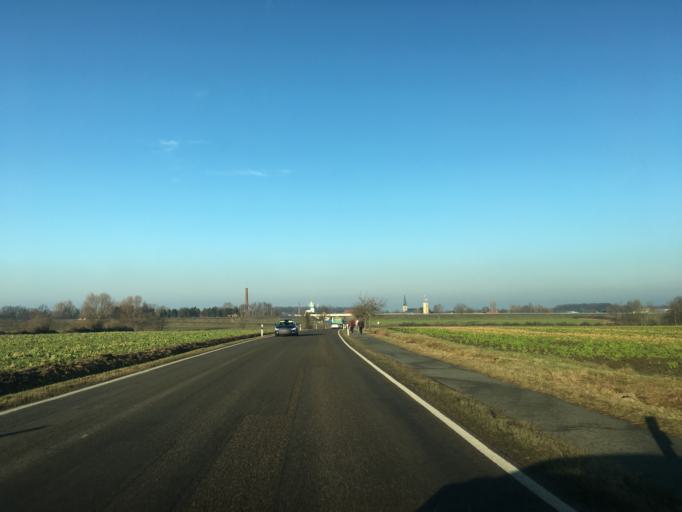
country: DE
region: North Rhine-Westphalia
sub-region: Regierungsbezirk Munster
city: Nordwalde
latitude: 52.0720
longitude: 7.4795
